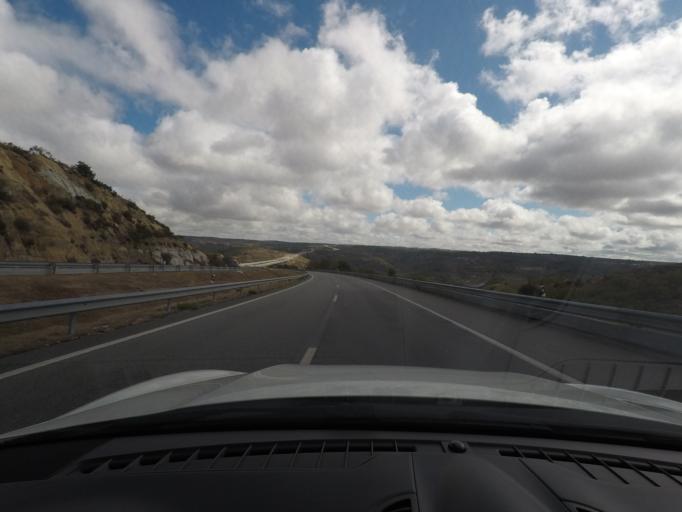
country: ES
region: Castille and Leon
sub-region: Provincia de Salamanca
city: Fuentes de Onoro
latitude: 40.6072
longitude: -6.9314
